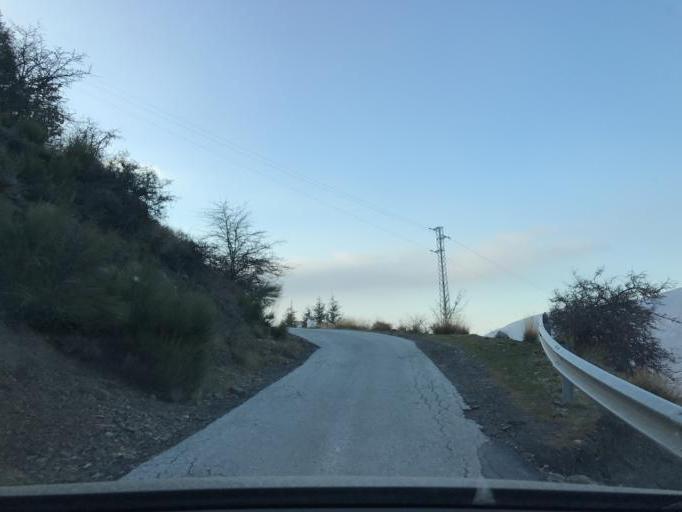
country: ES
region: Andalusia
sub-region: Provincia de Granada
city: Guejar-Sierra
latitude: 37.1370
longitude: -3.4202
